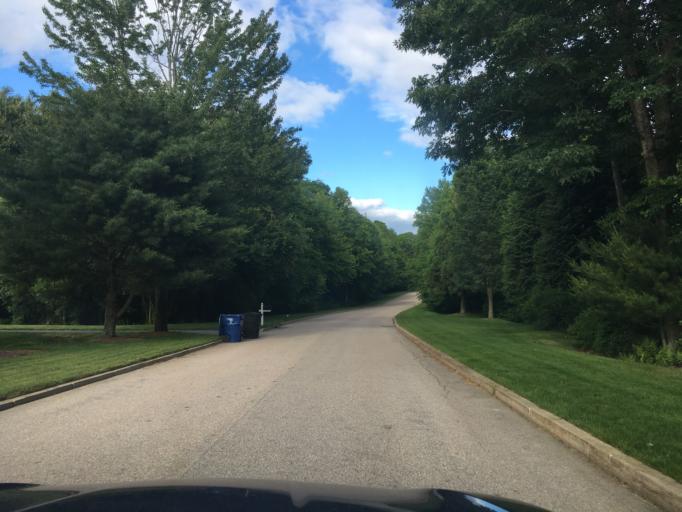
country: US
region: Rhode Island
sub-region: Washington County
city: Exeter
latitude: 41.6065
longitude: -71.5376
